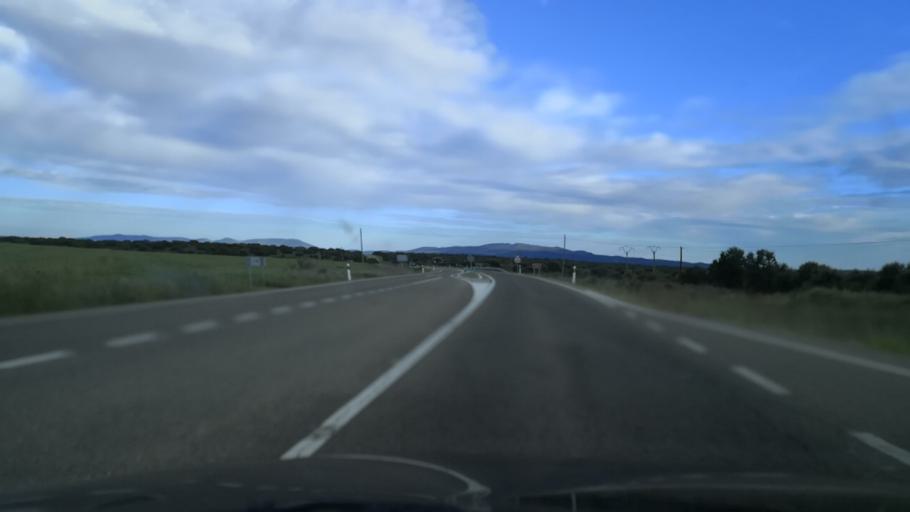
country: ES
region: Extremadura
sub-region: Provincia de Caceres
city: Torrejoncillo
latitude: 39.9299
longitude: -6.5040
